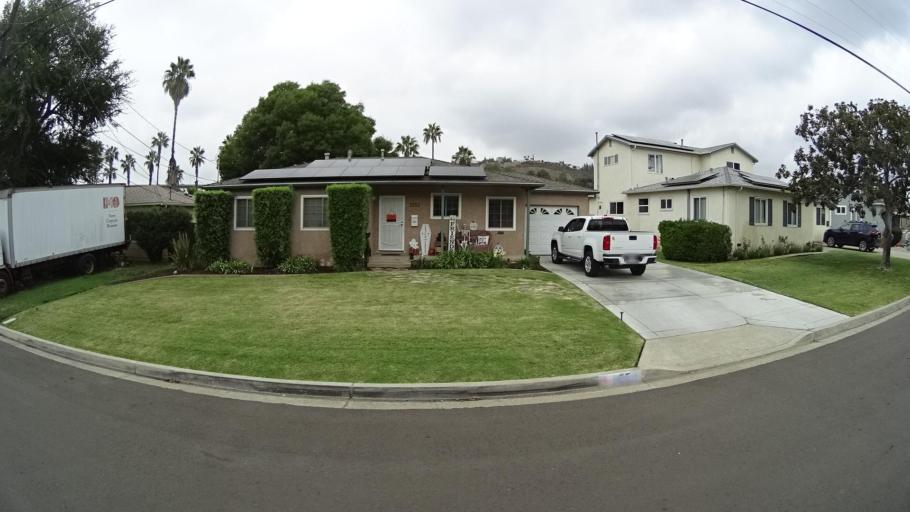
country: US
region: California
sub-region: San Diego County
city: Spring Valley
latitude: 32.7472
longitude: -117.0135
